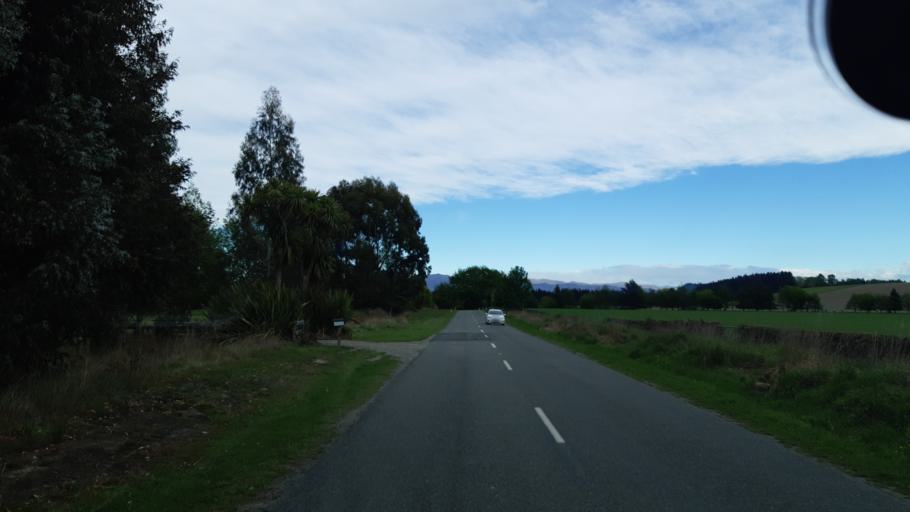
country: NZ
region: Canterbury
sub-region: Timaru District
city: Timaru
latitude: -44.4381
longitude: 171.1804
